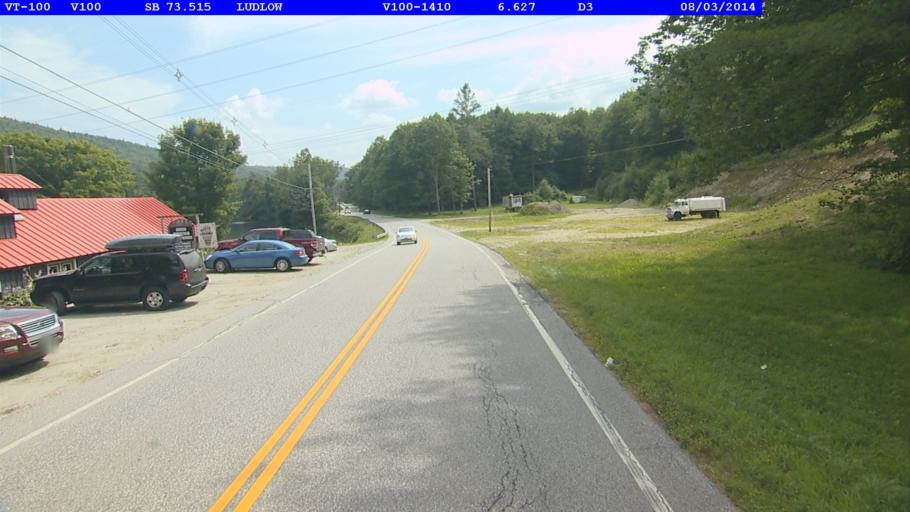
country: US
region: Vermont
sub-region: Windsor County
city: Chester
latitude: 43.4407
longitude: -72.6991
